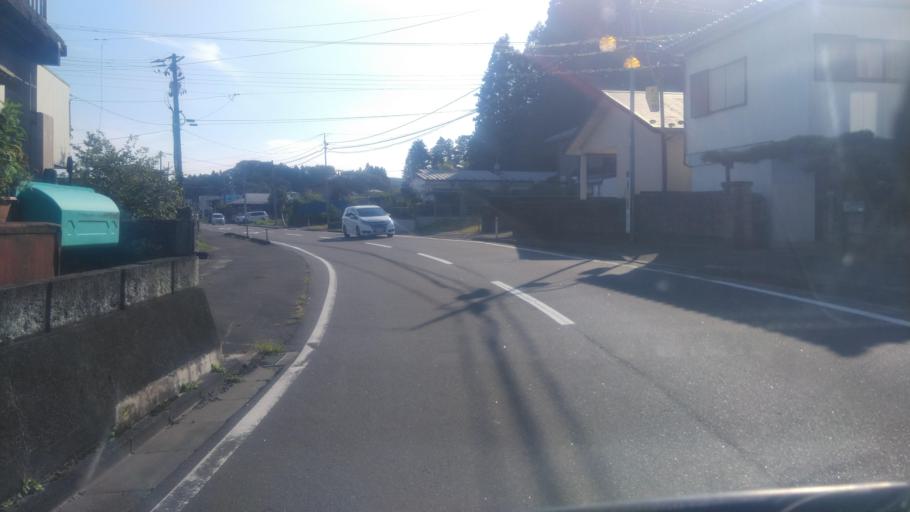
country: JP
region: Miyagi
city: Okawara
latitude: 38.1033
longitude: 140.6788
